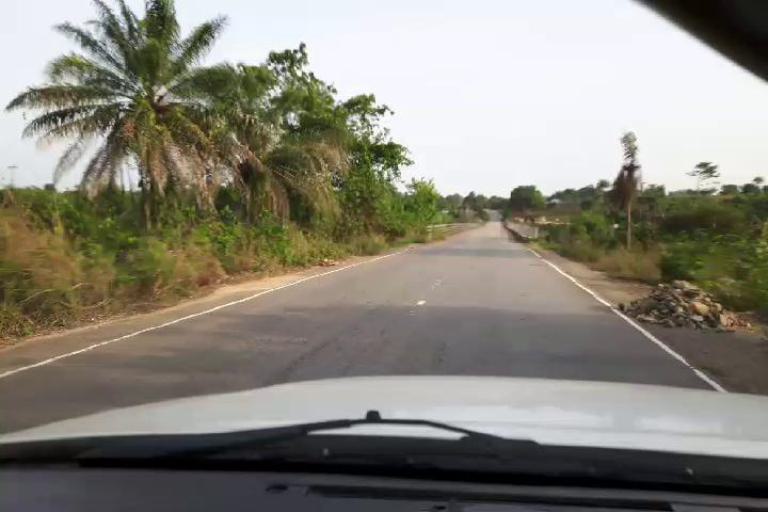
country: SL
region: Eastern Province
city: Blama
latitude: 7.9194
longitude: -11.4260
